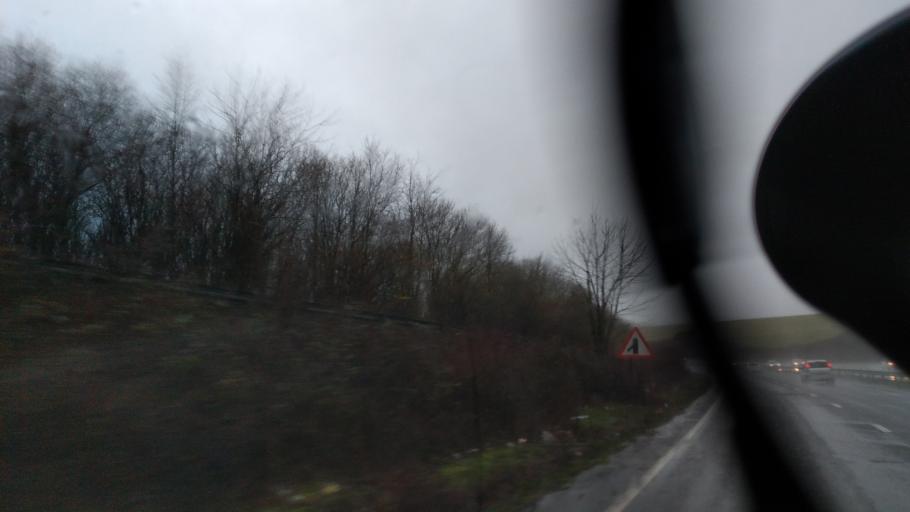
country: GB
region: England
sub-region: Brighton and Hove
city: Brighton
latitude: 50.8709
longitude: -0.1255
